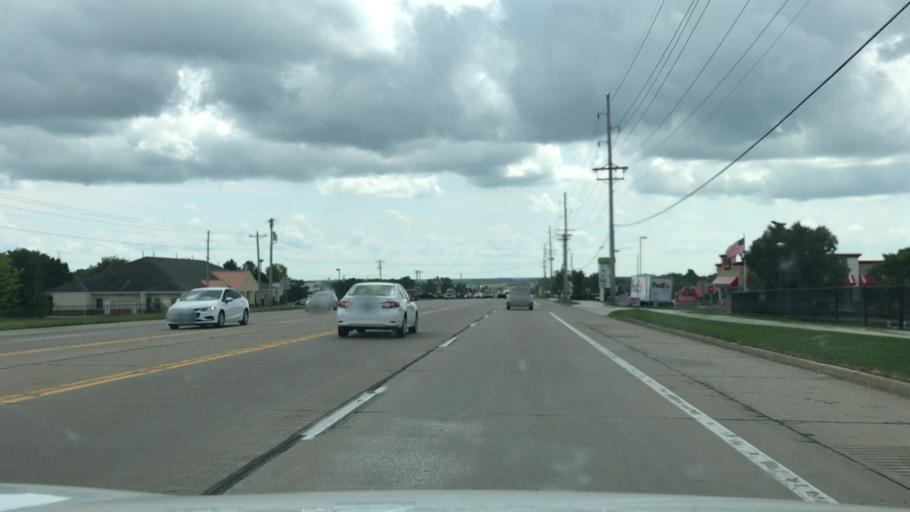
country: US
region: Missouri
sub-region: Saint Charles County
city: Dardenne Prairie
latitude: 38.7712
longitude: -90.7002
